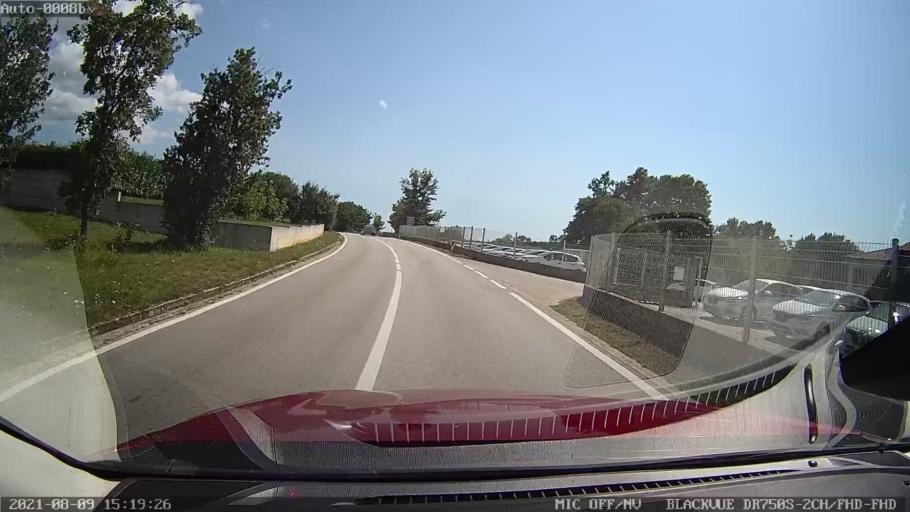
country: HR
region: Istarska
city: Pazin
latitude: 45.2148
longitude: 13.9015
